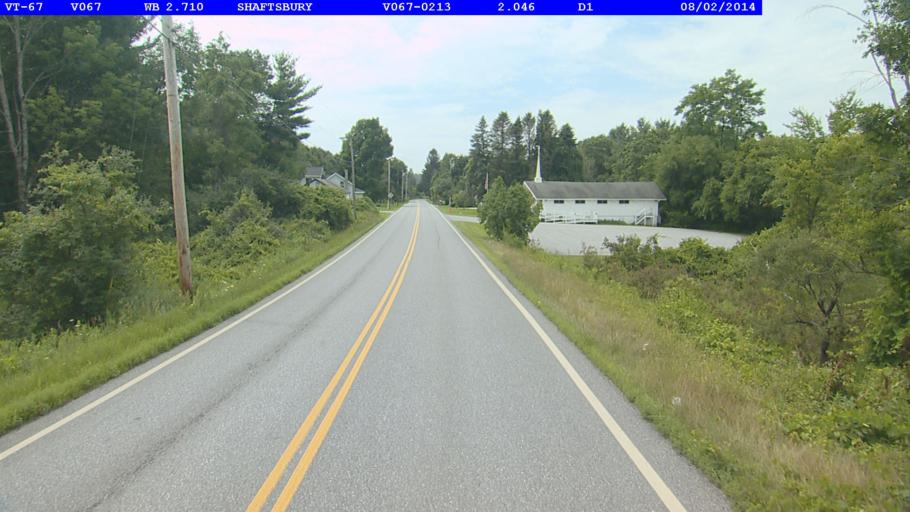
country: US
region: Vermont
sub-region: Bennington County
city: North Bennington
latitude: 42.9369
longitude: -73.2355
